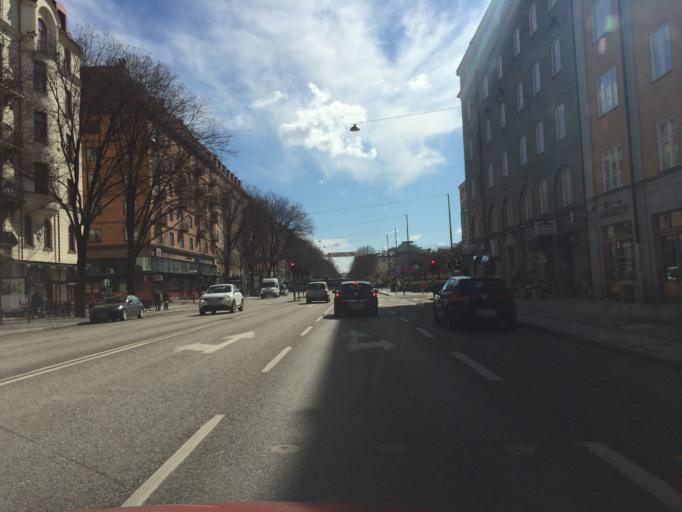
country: SE
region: Stockholm
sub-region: Stockholms Kommun
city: Stockholm
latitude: 59.3452
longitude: 18.0543
